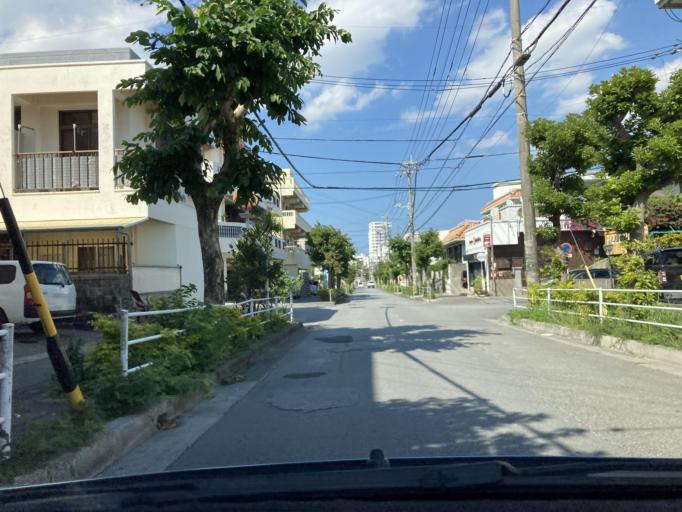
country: JP
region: Okinawa
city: Naha-shi
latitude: 26.2015
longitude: 127.6905
